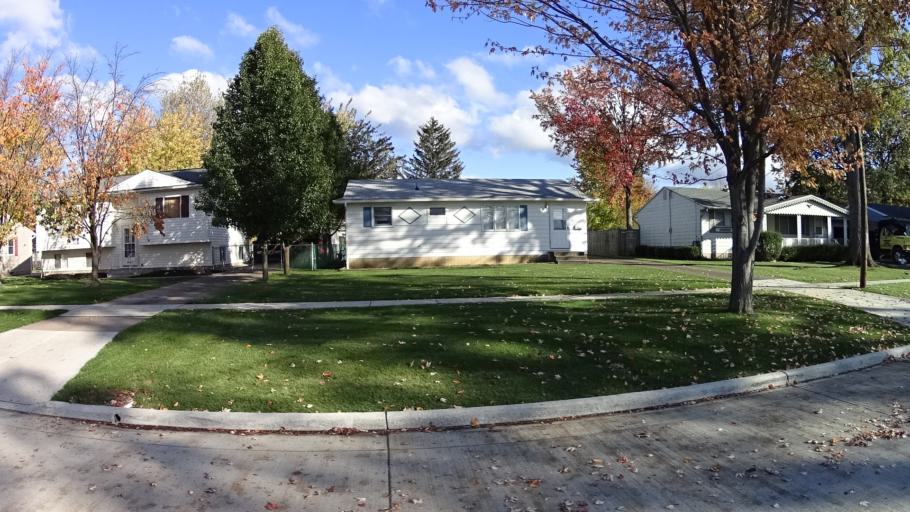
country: US
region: Ohio
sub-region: Lorain County
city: Sheffield
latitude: 41.4333
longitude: -82.1317
